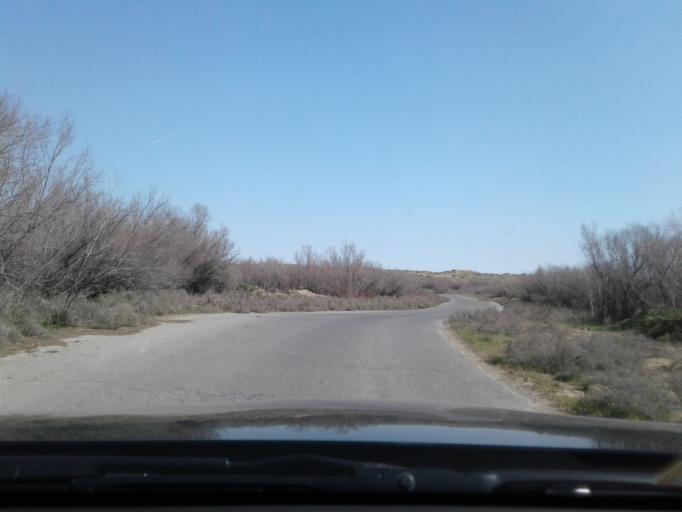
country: TM
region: Ahal
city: Abadan
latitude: 38.1464
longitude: 58.1947
